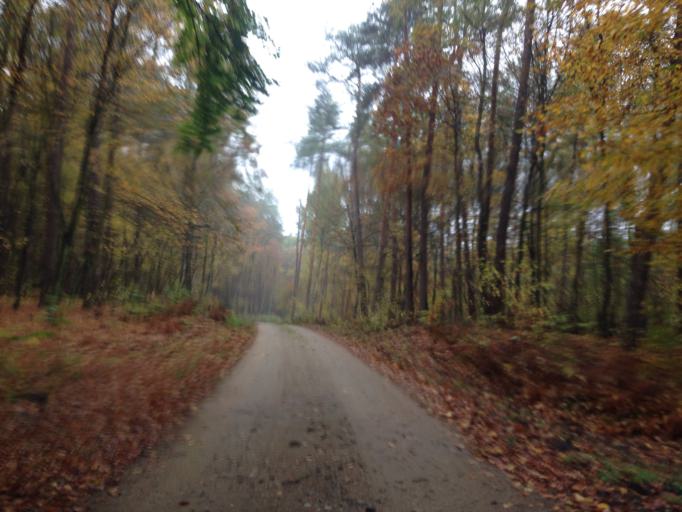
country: PL
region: Warmian-Masurian Voivodeship
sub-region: Powiat dzialdowski
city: Lidzbark
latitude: 53.2699
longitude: 19.7324
